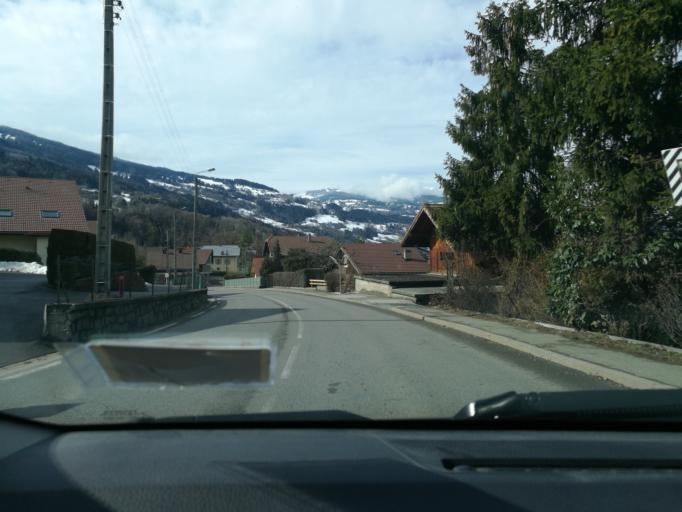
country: FR
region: Rhone-Alpes
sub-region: Departement de la Haute-Savoie
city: Saint-Gervais-les-Bains
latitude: 45.9068
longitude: 6.7096
